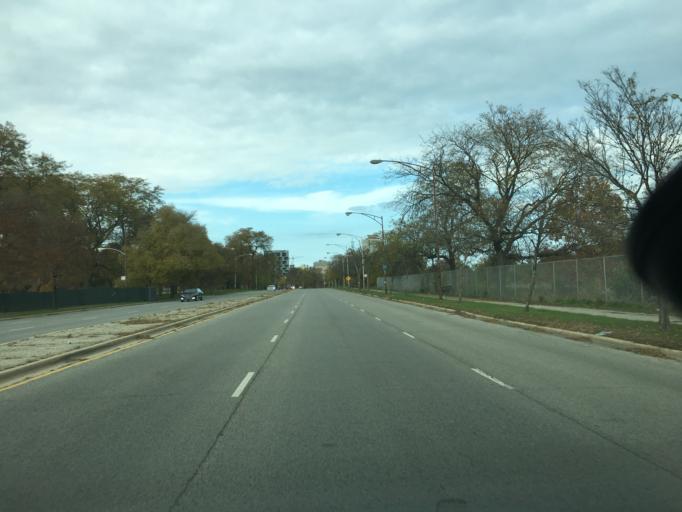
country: US
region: Illinois
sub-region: Cook County
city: Chicago
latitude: 41.7815
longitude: -87.5844
